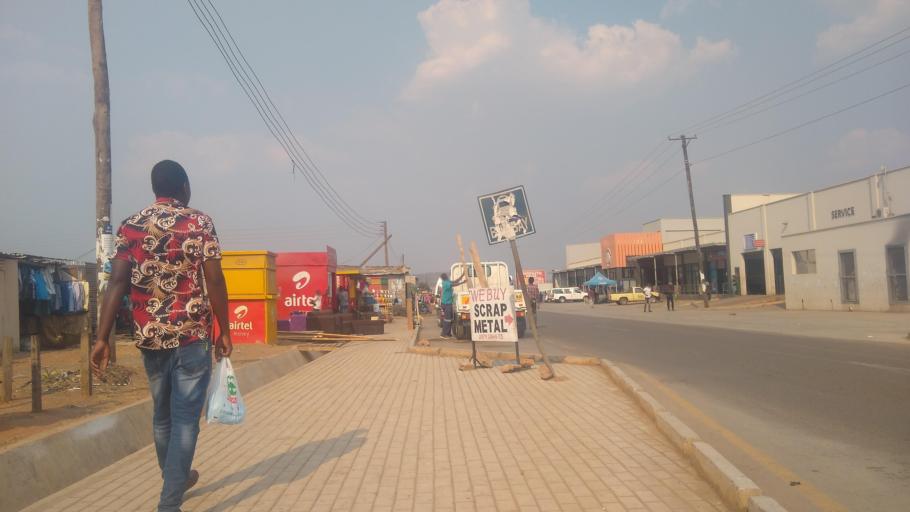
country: ZM
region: Lusaka
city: Lusaka
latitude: -15.4480
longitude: 28.3745
